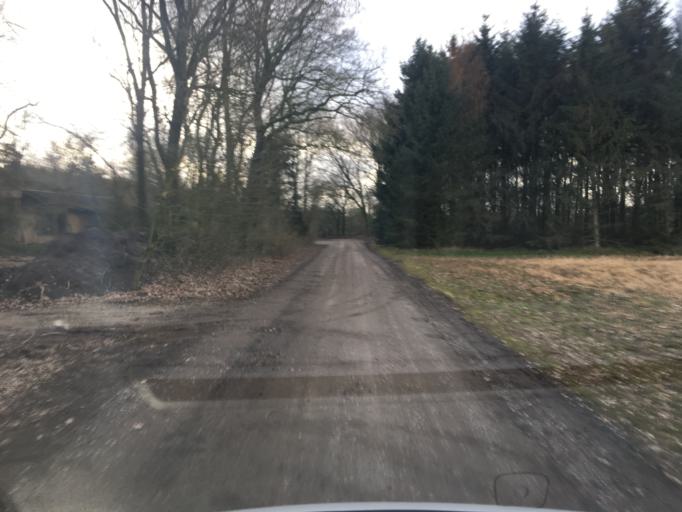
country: DK
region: South Denmark
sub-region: Aabenraa Kommune
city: Krusa
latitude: 54.8994
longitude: 9.4769
